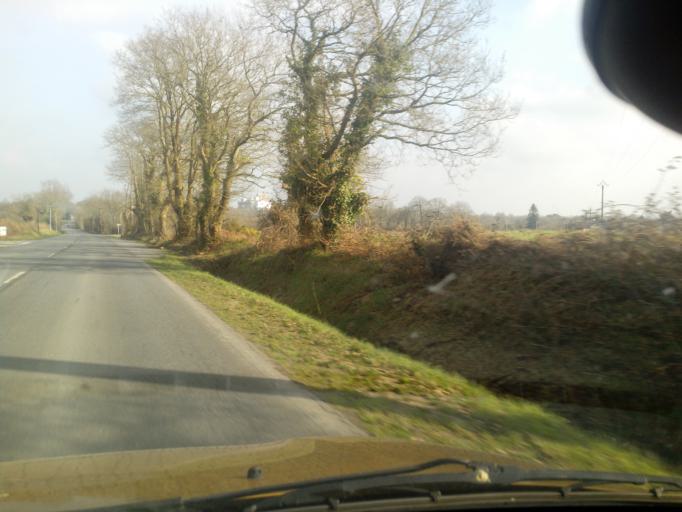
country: FR
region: Brittany
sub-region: Departement du Morbihan
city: Questembert
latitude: 47.6896
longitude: -2.4727
